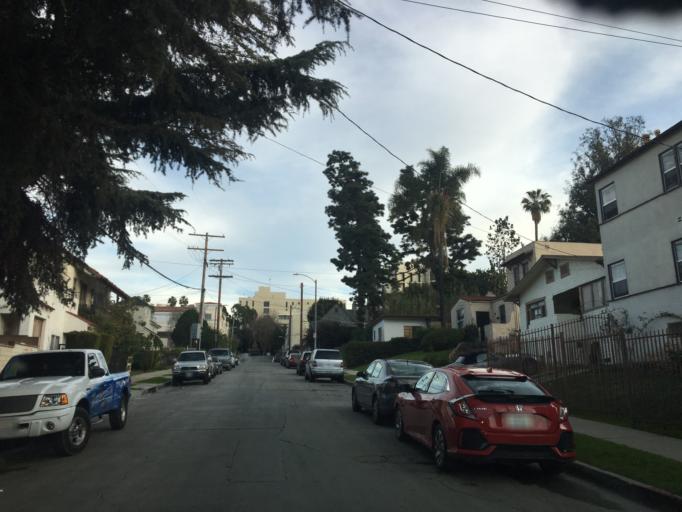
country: US
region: California
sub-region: Los Angeles County
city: Echo Park
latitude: 34.0655
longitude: -118.2755
